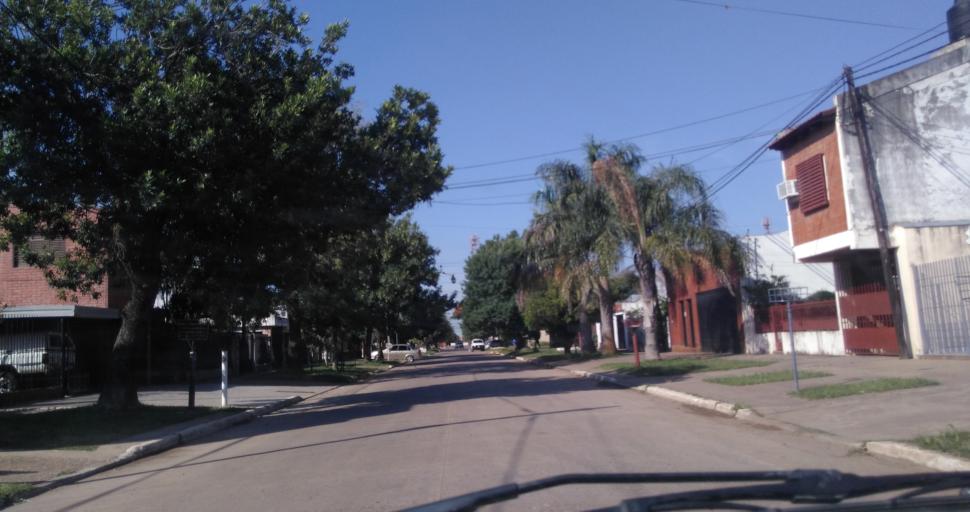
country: AR
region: Chaco
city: Resistencia
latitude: -27.4680
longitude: -58.9642
